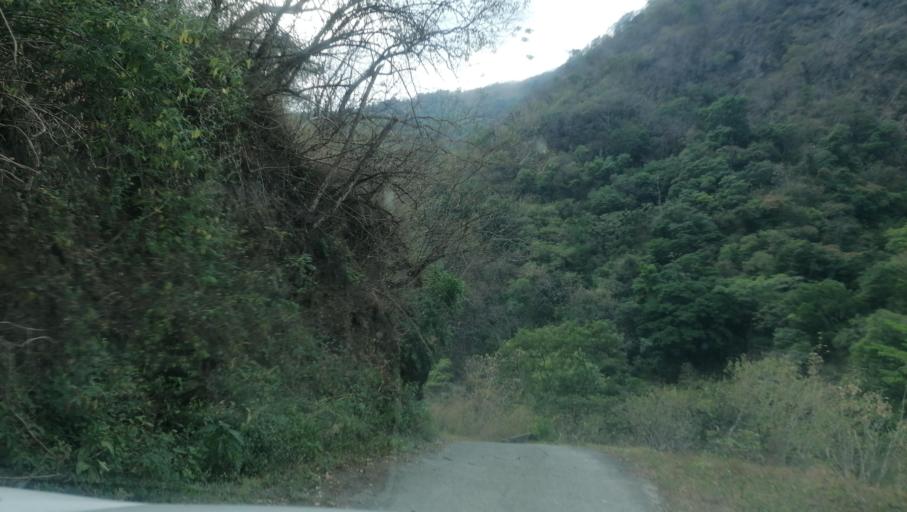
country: MX
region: Chiapas
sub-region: Cacahoatan
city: Benito Juarez
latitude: 15.1577
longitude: -92.1795
